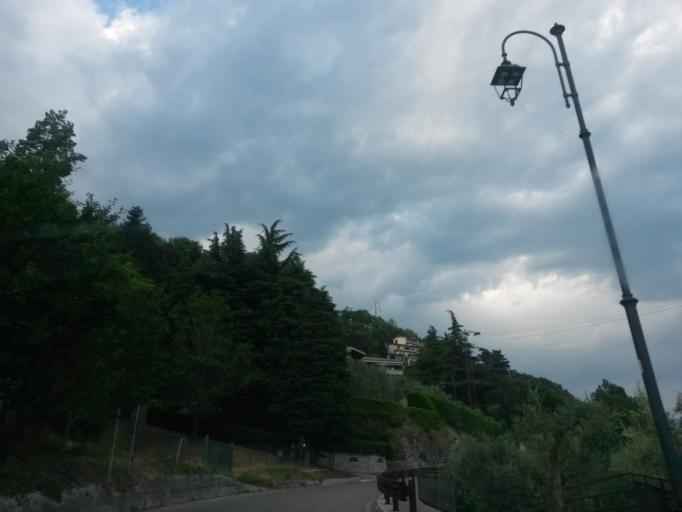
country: IT
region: Lombardy
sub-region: Provincia di Brescia
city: Gardola
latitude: 45.7366
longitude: 10.7241
